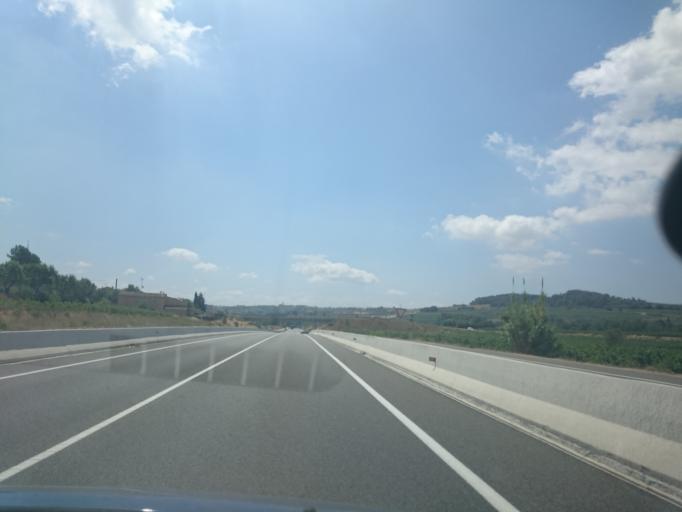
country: ES
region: Catalonia
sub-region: Provincia de Barcelona
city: el Pla del Penedes
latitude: 41.4007
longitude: 1.7056
